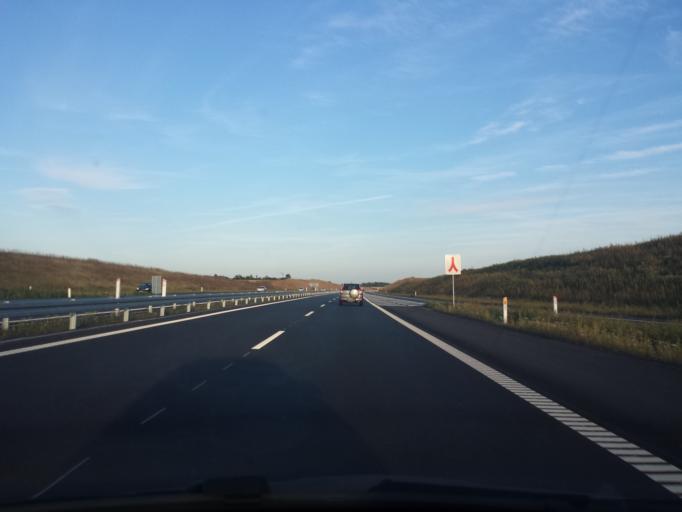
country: DK
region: Capital Region
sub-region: Egedal Kommune
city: Smorumnedre
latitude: 55.7165
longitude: 12.3157
